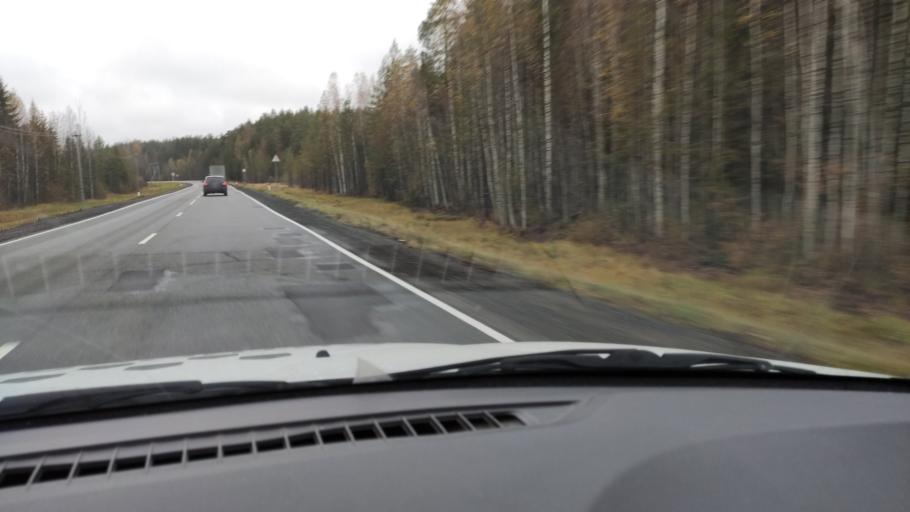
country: RU
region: Kirov
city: Belaya Kholunitsa
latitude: 58.9087
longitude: 50.9885
